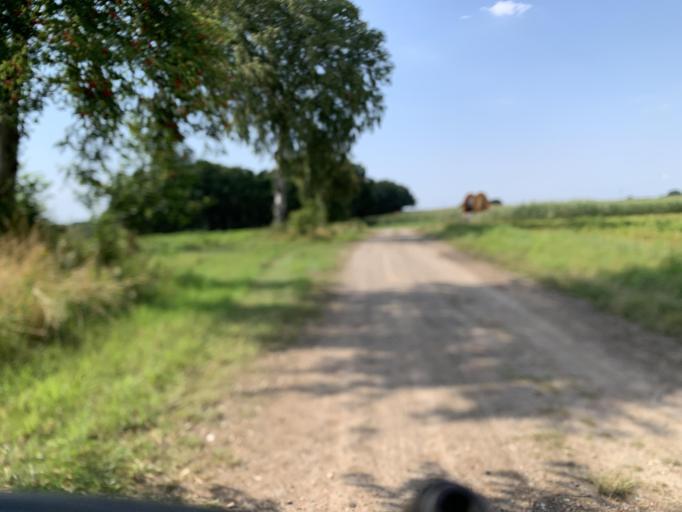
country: DE
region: Lower Saxony
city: Thomasburg
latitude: 53.2328
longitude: 10.6400
